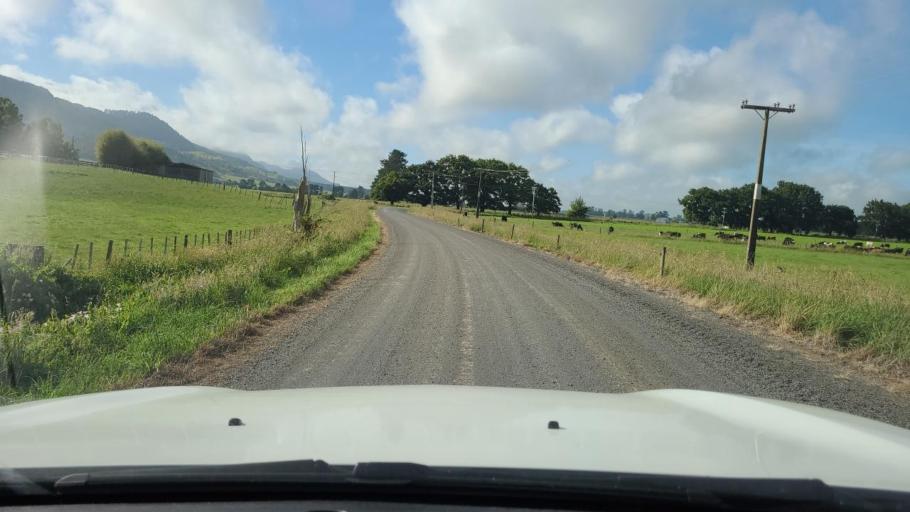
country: NZ
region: Bay of Plenty
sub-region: Western Bay of Plenty District
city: Katikati
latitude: -37.6142
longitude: 175.7955
